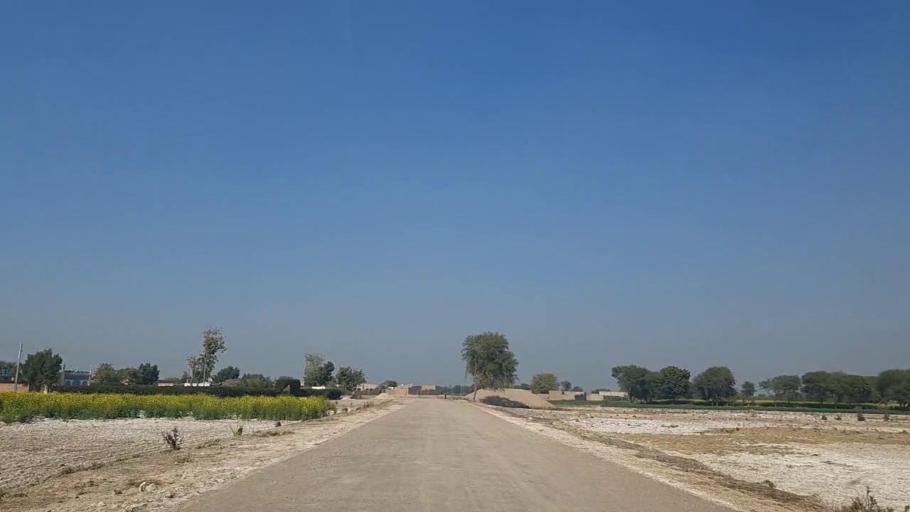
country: PK
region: Sindh
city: Nawabshah
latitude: 26.2278
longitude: 68.3435
